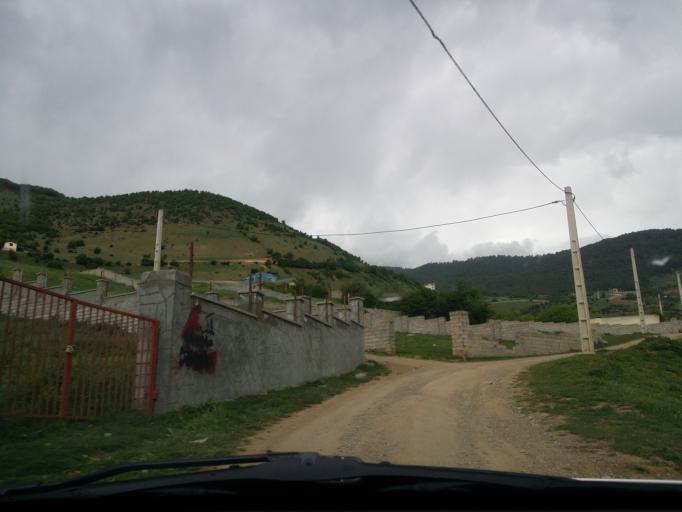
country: IR
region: Mazandaran
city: `Abbasabad
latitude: 36.5069
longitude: 51.1408
